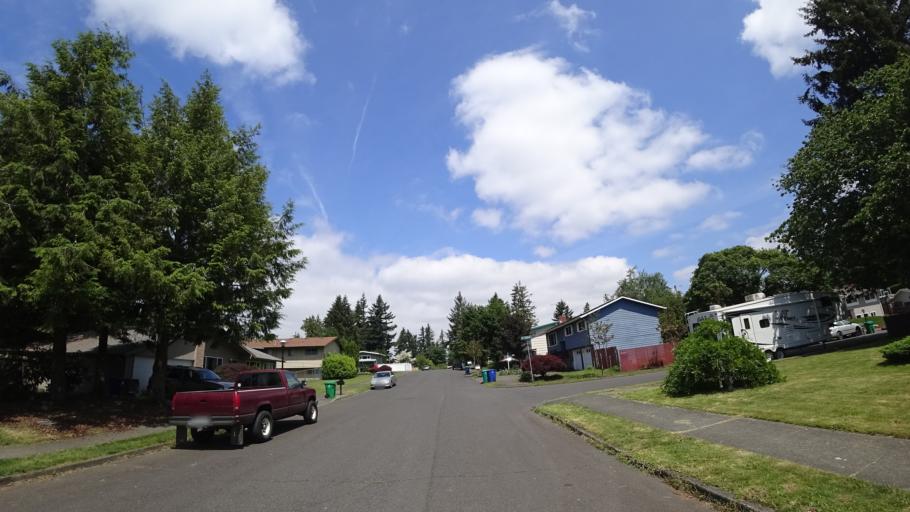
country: US
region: Oregon
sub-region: Multnomah County
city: Gresham
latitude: 45.4986
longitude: -122.4906
